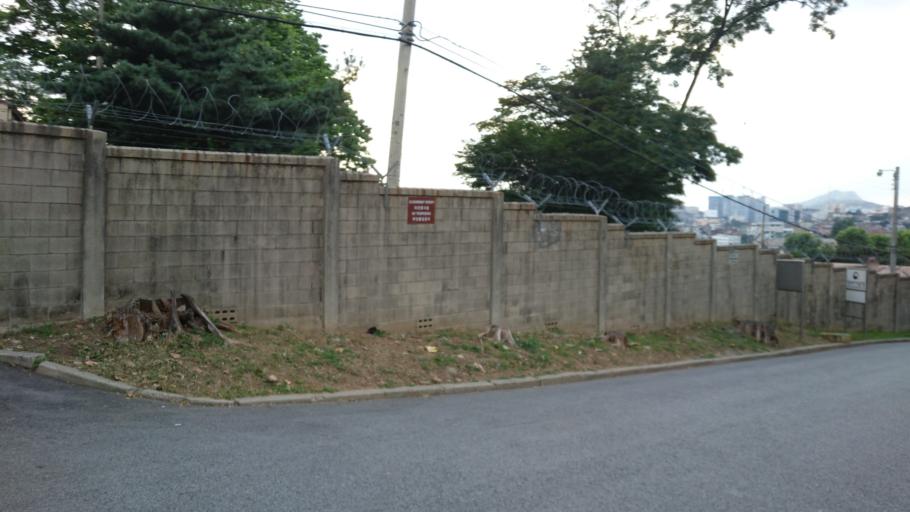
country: KR
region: Seoul
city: Seoul
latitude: 37.5415
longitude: 126.9795
